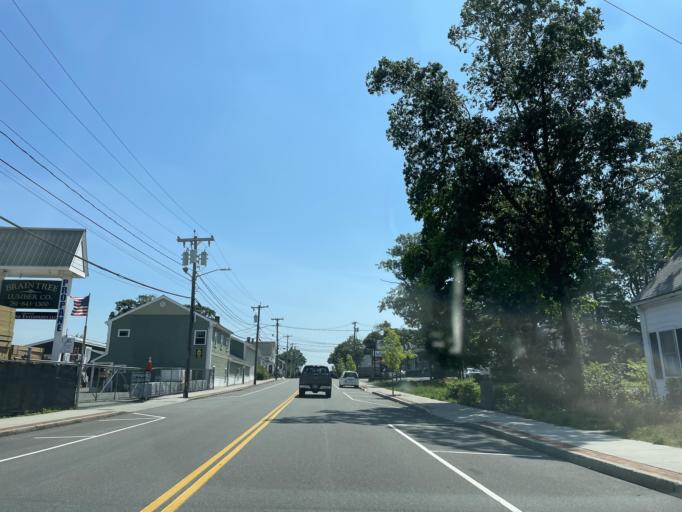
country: US
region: Massachusetts
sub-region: Norfolk County
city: Braintree
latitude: 42.1999
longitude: -71.0051
